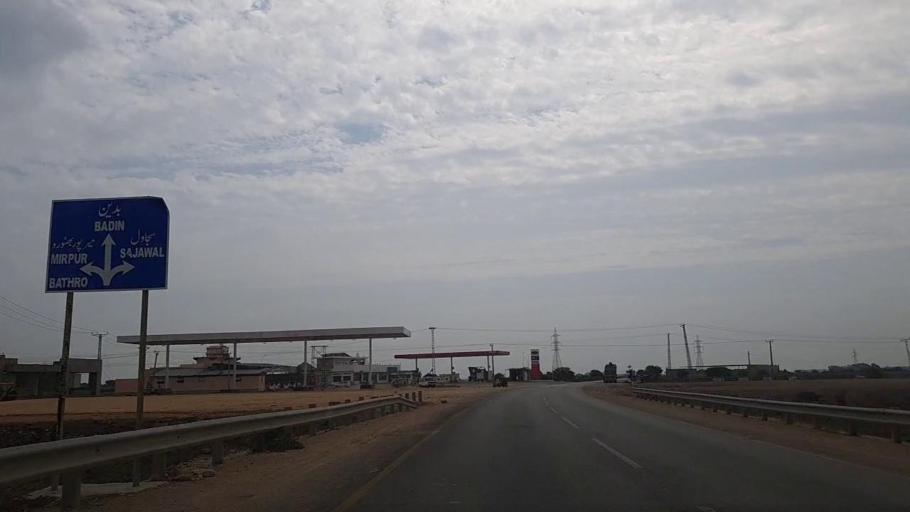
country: PK
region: Sindh
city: Daro Mehar
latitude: 24.6155
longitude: 68.0886
